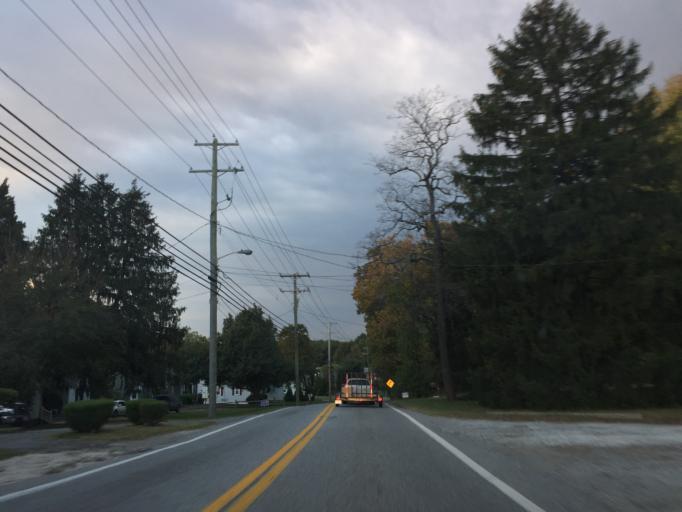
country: US
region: Maryland
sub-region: Baltimore County
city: White Marsh
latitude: 39.3758
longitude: -76.4195
